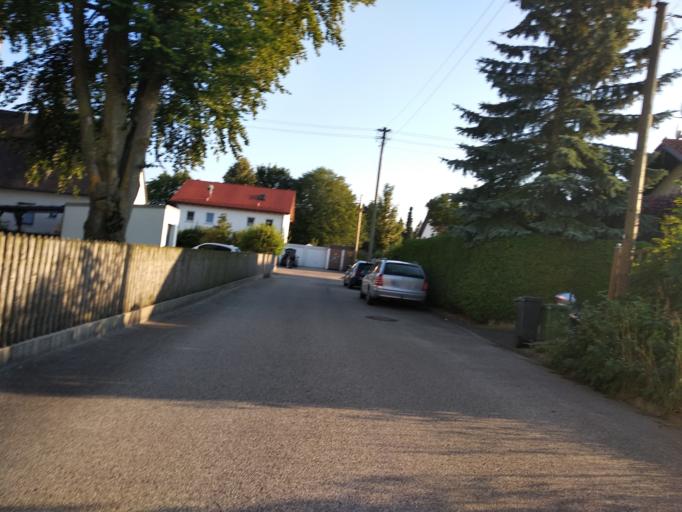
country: DE
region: Bavaria
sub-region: Upper Bavaria
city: Forstinning
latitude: 48.1684
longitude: 11.9164
